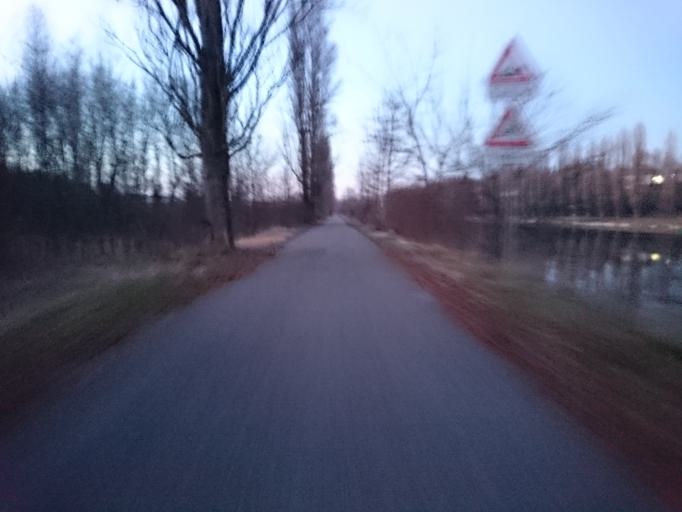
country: IT
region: Veneto
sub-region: Provincia di Verona
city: Salionze
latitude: 45.4101
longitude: 10.7166
